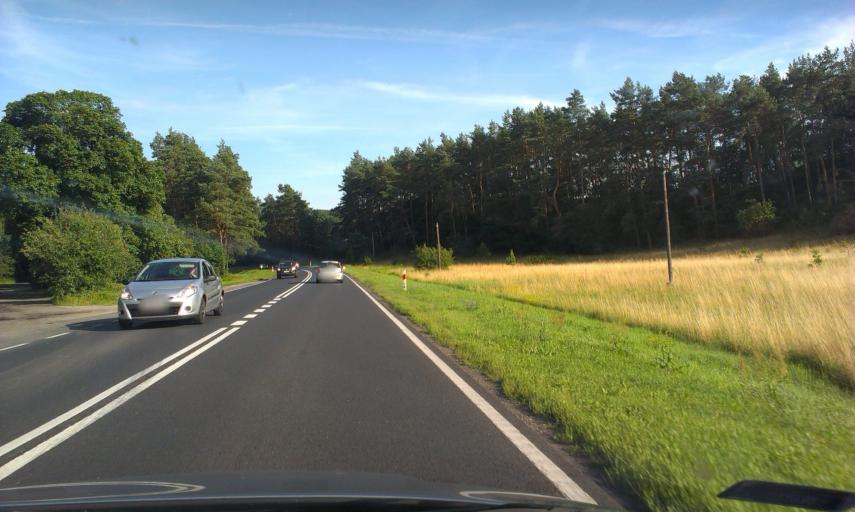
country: PL
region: Kujawsko-Pomorskie
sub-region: Powiat bydgoski
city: Sicienko
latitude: 53.1622
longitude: 17.7912
